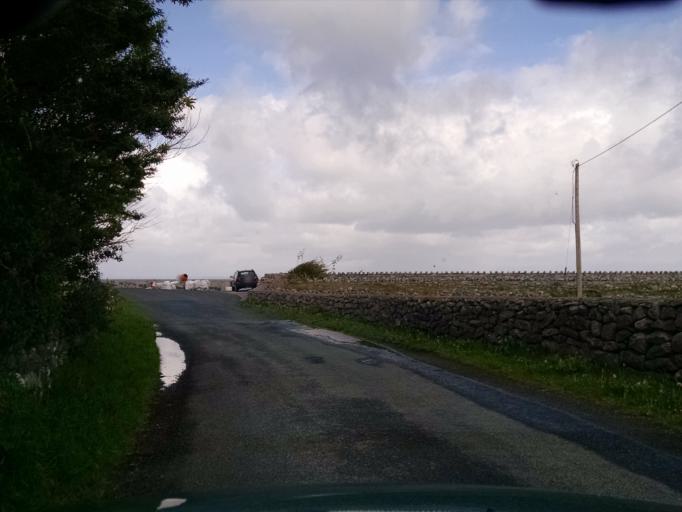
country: IE
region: Connaught
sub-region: County Galway
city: Bearna
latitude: 53.1567
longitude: -9.0854
